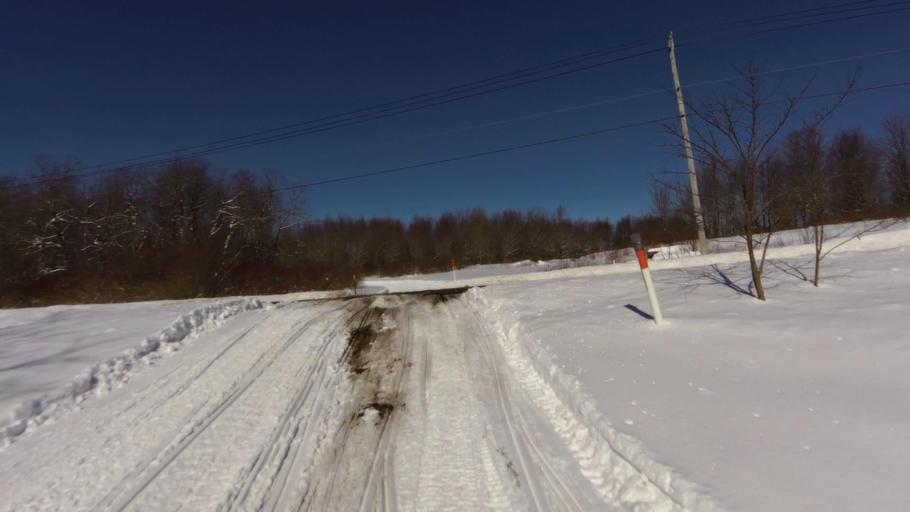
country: US
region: New York
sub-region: Chautauqua County
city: Lakewood
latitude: 42.2281
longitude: -79.3461
